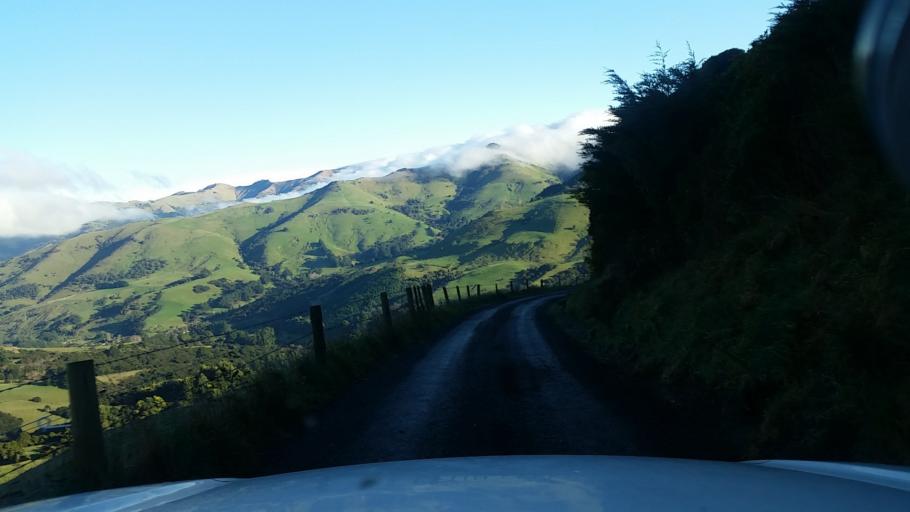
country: NZ
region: Canterbury
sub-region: Christchurch City
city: Christchurch
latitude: -43.7474
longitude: 172.8595
